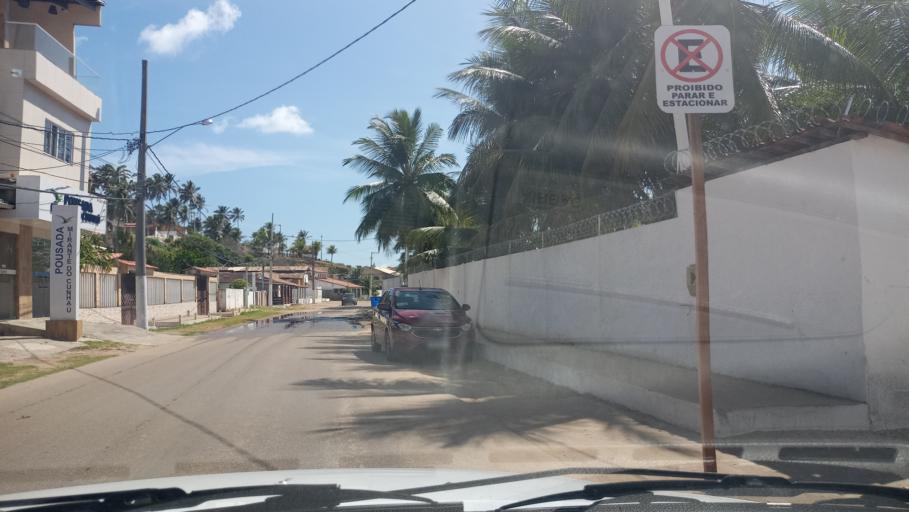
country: BR
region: Rio Grande do Norte
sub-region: Canguaretama
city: Canguaretama
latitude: -6.3131
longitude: -35.0414
